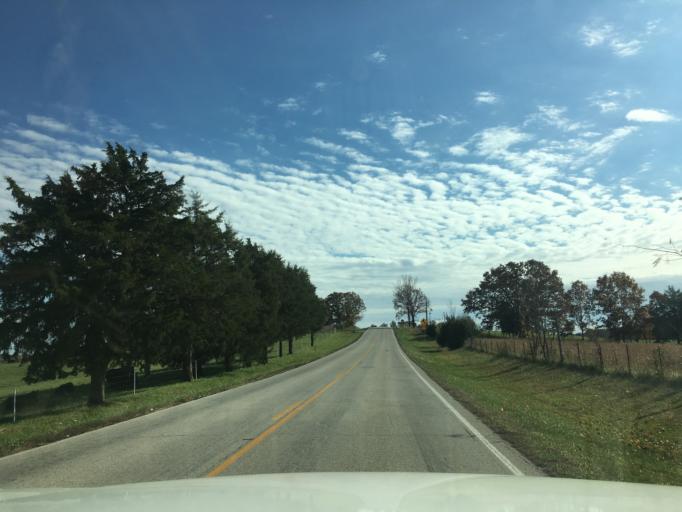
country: US
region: Missouri
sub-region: Maries County
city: Belle
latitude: 38.3451
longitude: -91.7933
